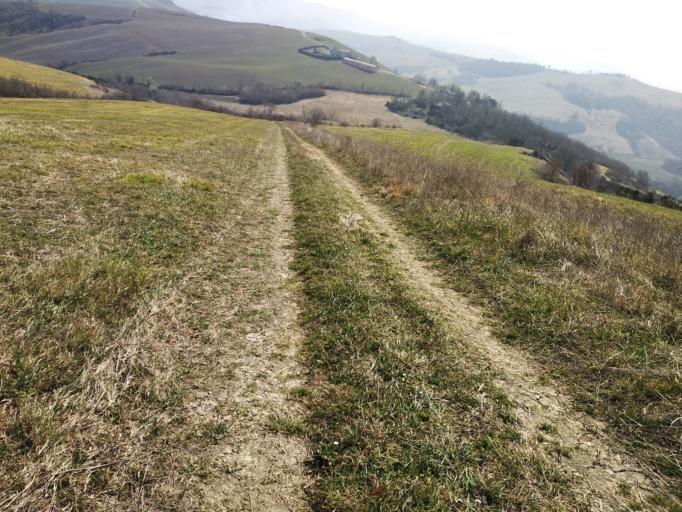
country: IT
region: Emilia-Romagna
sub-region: Provincia di Bologna
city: Osteria Grande
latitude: 44.3632
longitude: 11.5163
